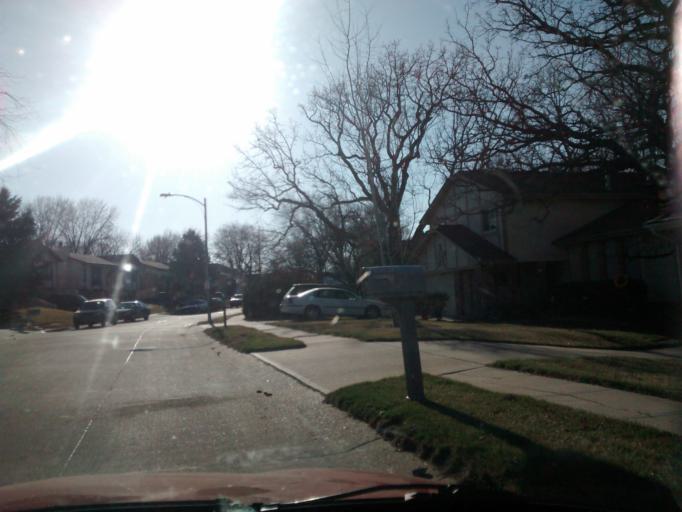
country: US
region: Nebraska
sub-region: Sarpy County
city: Offutt Air Force Base
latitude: 41.1152
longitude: -95.9690
